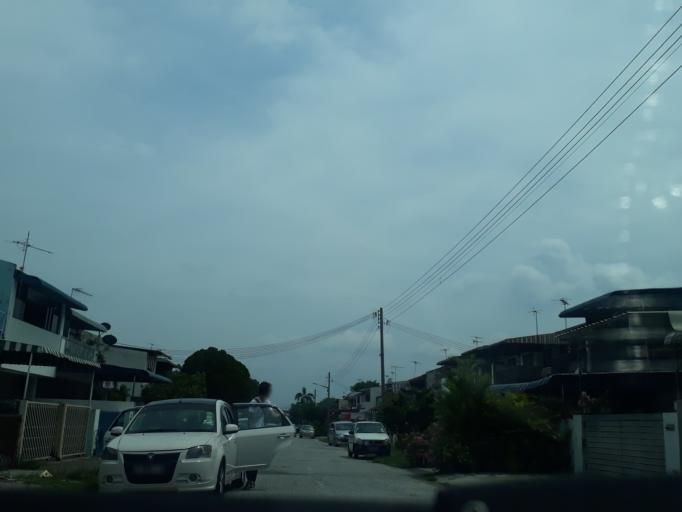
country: MY
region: Perak
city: Ipoh
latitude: 4.5935
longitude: 101.1329
